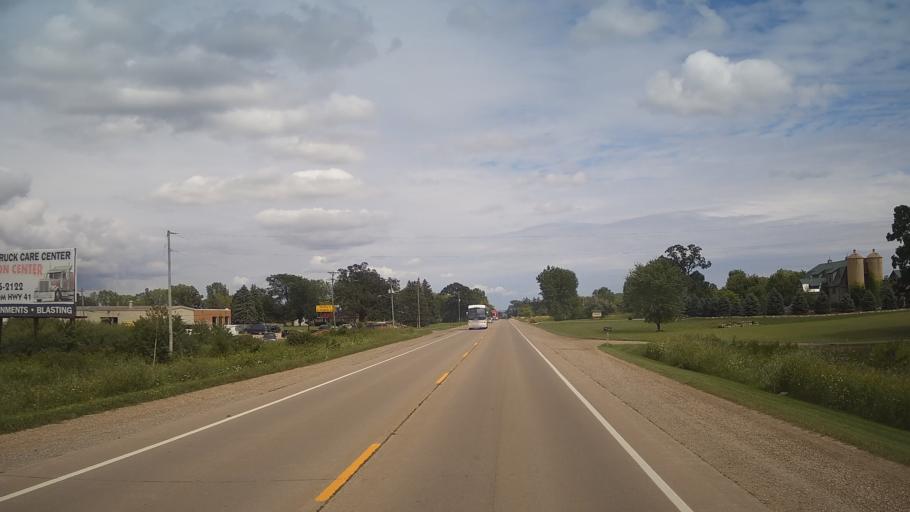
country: US
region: Wisconsin
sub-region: Winnebago County
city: Oshkosh
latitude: 44.0331
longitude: -88.6408
